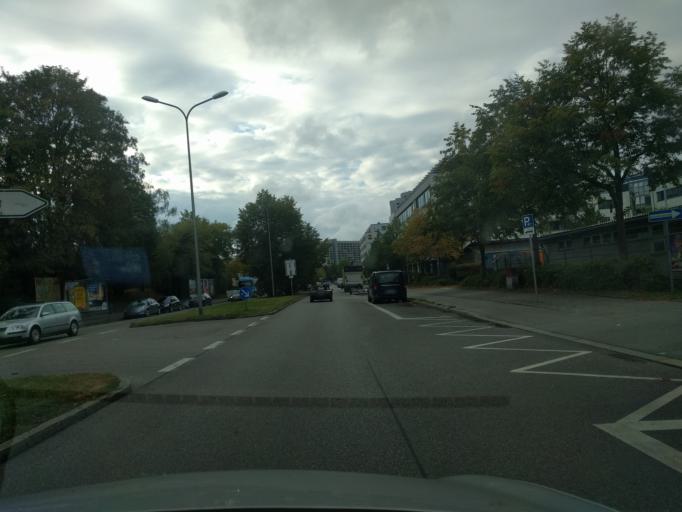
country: DE
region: Bavaria
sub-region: Upper Bavaria
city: Munich
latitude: 48.1317
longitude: 11.5264
